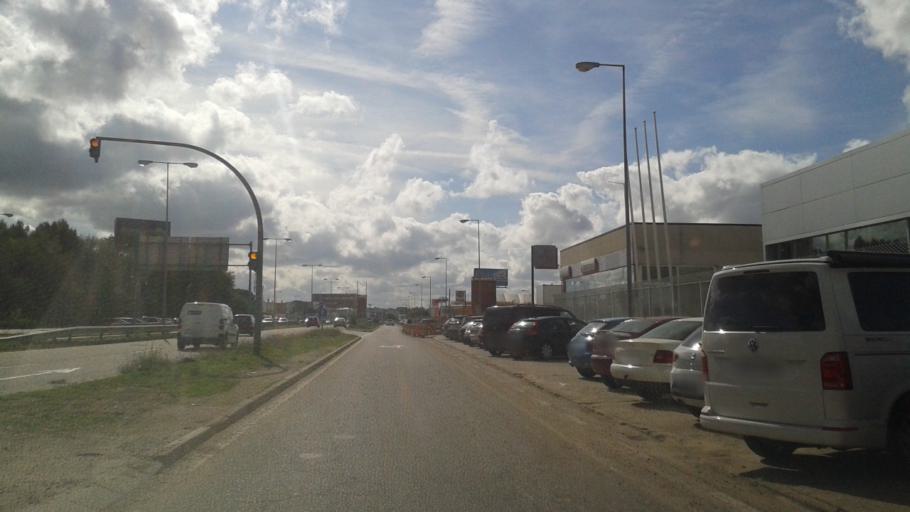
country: ES
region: Castille and Leon
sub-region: Provincia de Valladolid
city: Valladolid
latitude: 41.6764
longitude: -4.7229
